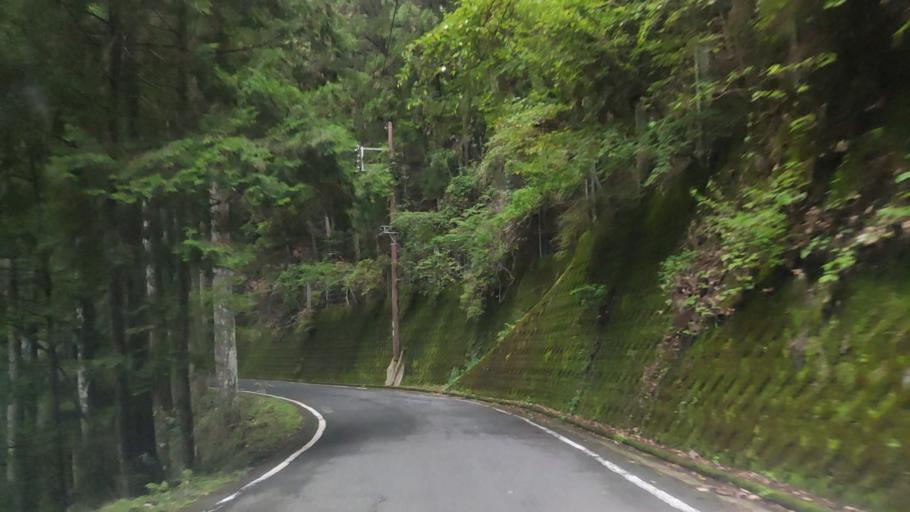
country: JP
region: Wakayama
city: Koya
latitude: 34.2342
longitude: 135.6452
